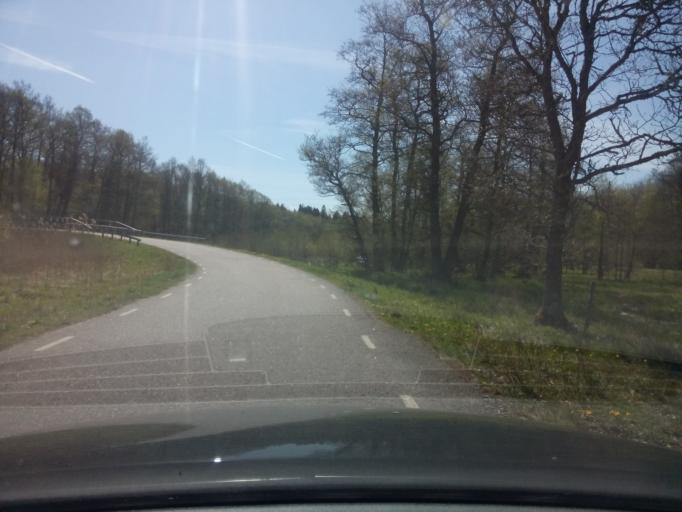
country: SE
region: Soedermanland
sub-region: Trosa Kommun
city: Trosa
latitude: 58.8048
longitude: 17.3643
